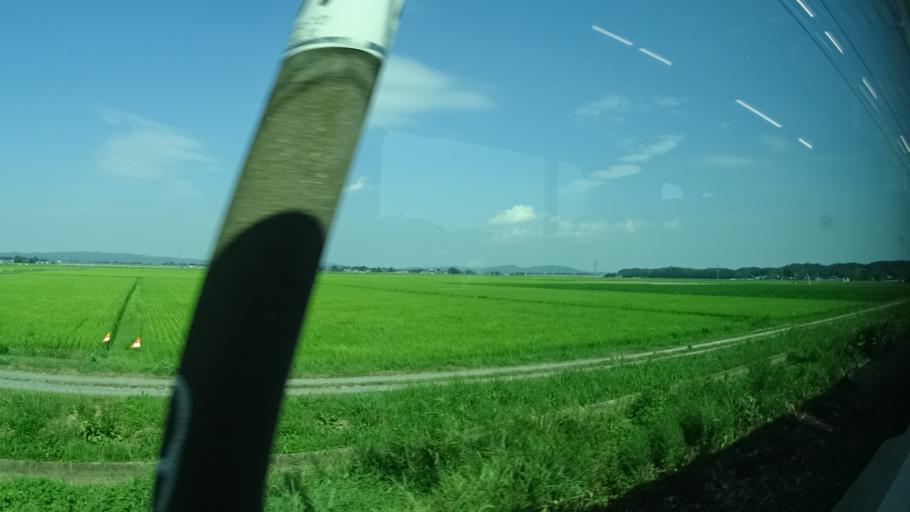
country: JP
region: Miyagi
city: Kogota
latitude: 38.5088
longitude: 141.0779
